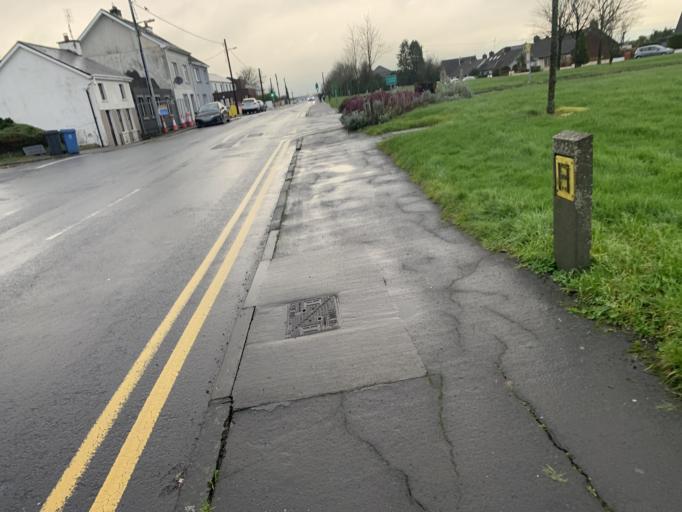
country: IE
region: Connaught
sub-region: County Galway
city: Tuam
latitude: 53.5197
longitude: -8.8525
